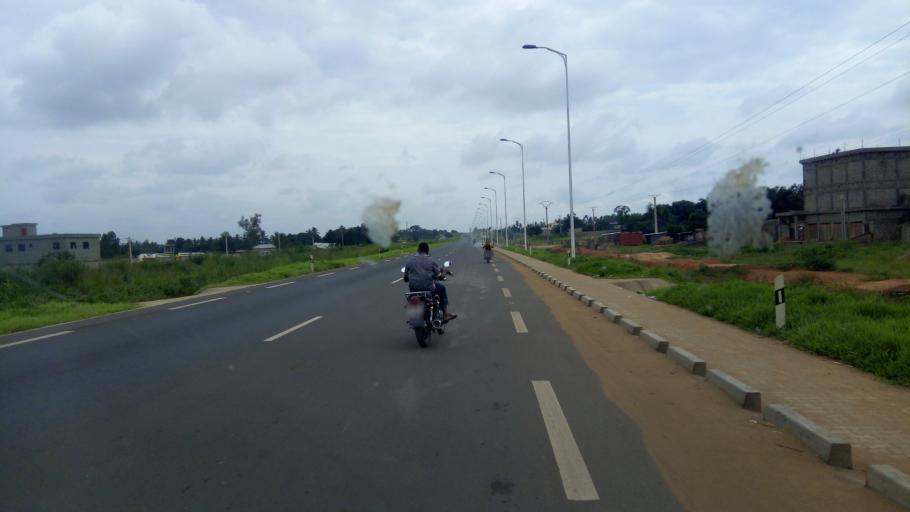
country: TG
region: Maritime
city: Tsevie
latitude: 6.3287
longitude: 1.2185
